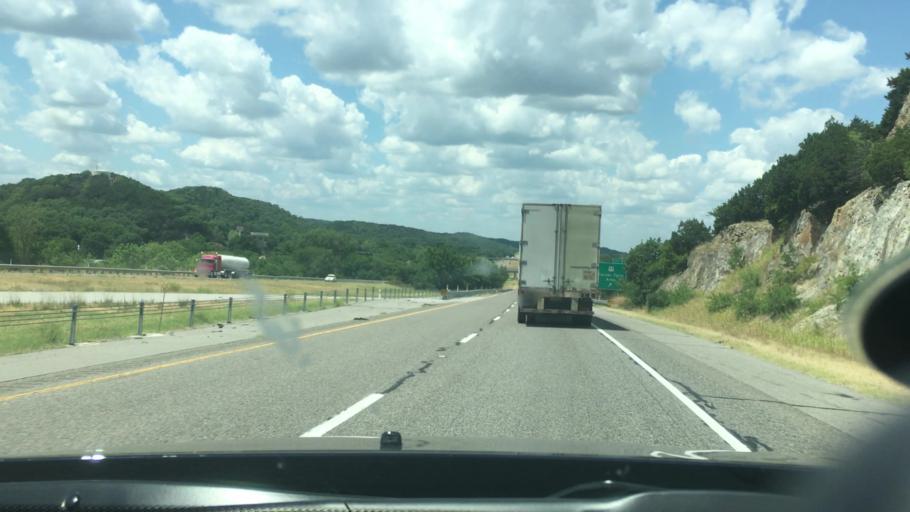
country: US
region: Oklahoma
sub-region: Murray County
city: Davis
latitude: 34.4457
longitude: -97.1303
